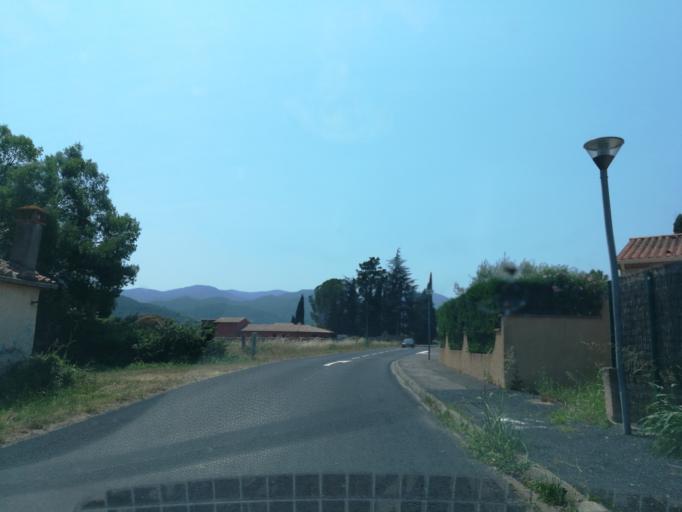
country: FR
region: Languedoc-Roussillon
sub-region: Departement des Pyrenees-Orientales
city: Maureillas-las-Illas
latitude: 42.4927
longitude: 2.8023
